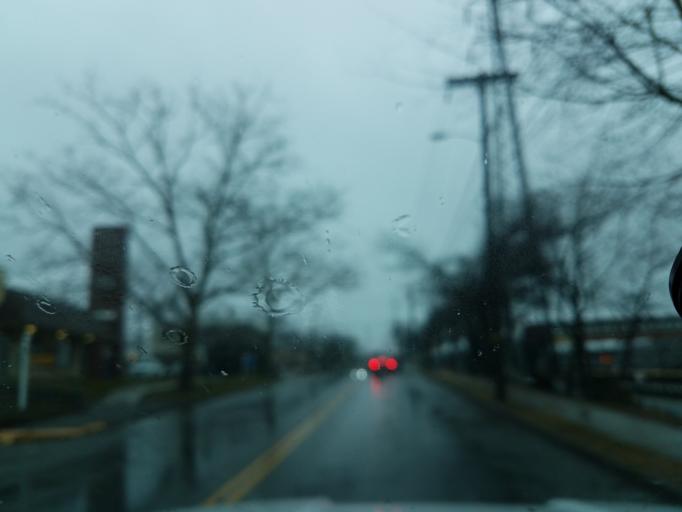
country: US
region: Connecticut
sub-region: Fairfield County
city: Darien
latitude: 41.0693
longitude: -73.4980
